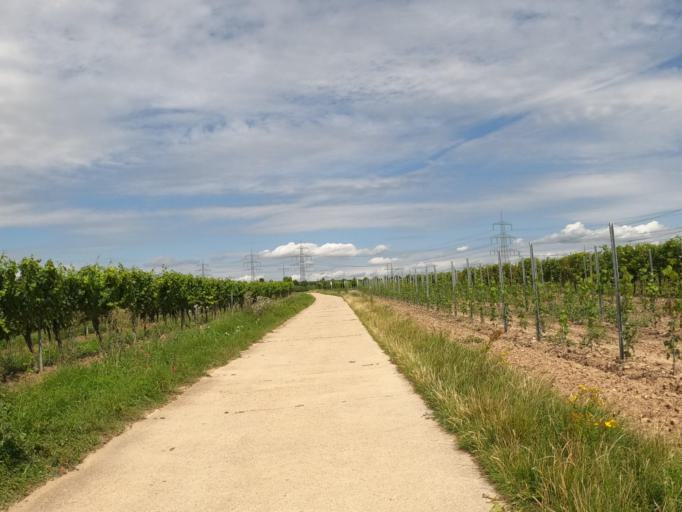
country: DE
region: Rheinland-Pfalz
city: Grosskarlbach
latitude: 49.5446
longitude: 8.2215
